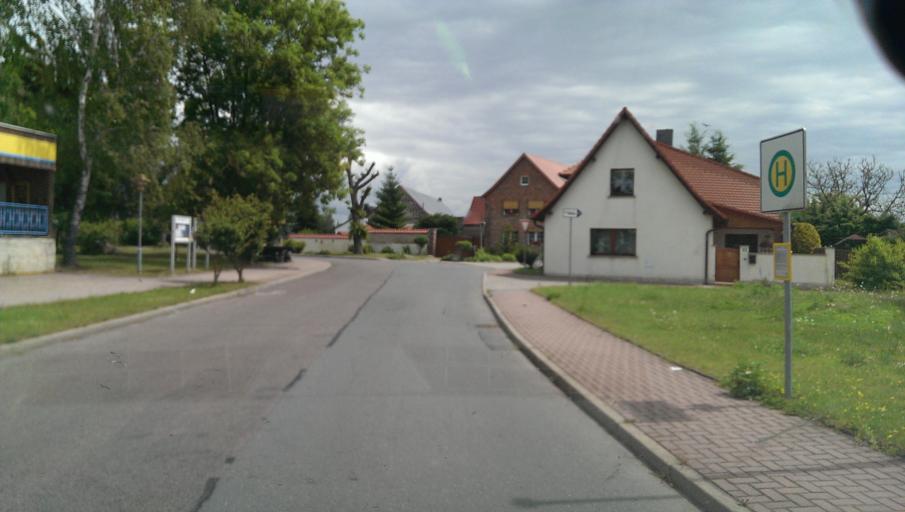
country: DE
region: Saxony-Anhalt
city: Farnstadt
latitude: 51.4287
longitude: 11.5707
